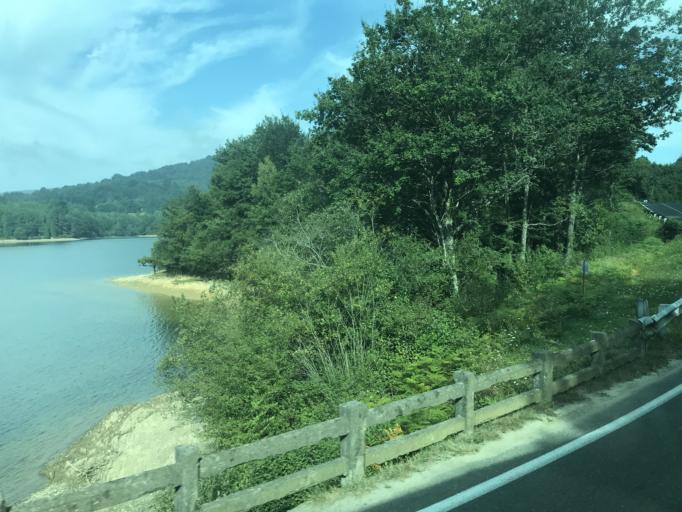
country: ES
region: Basque Country
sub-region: Bizkaia
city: Otxandio
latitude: 43.0069
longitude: -2.6436
